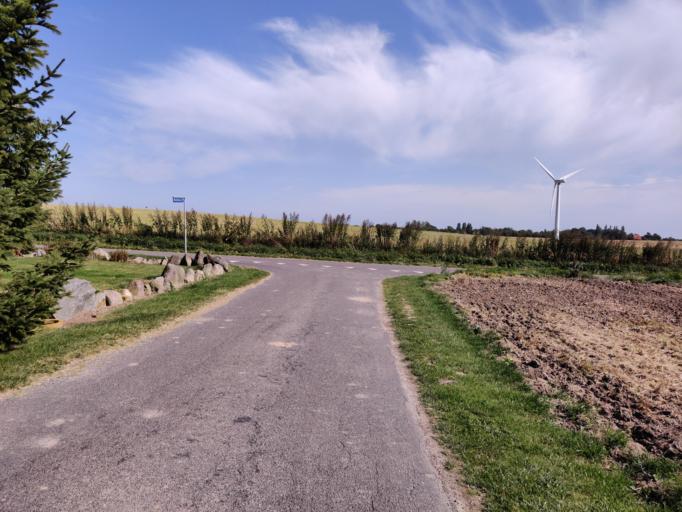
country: DK
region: Zealand
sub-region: Guldborgsund Kommune
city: Nykobing Falster
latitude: 54.6814
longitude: 11.8907
